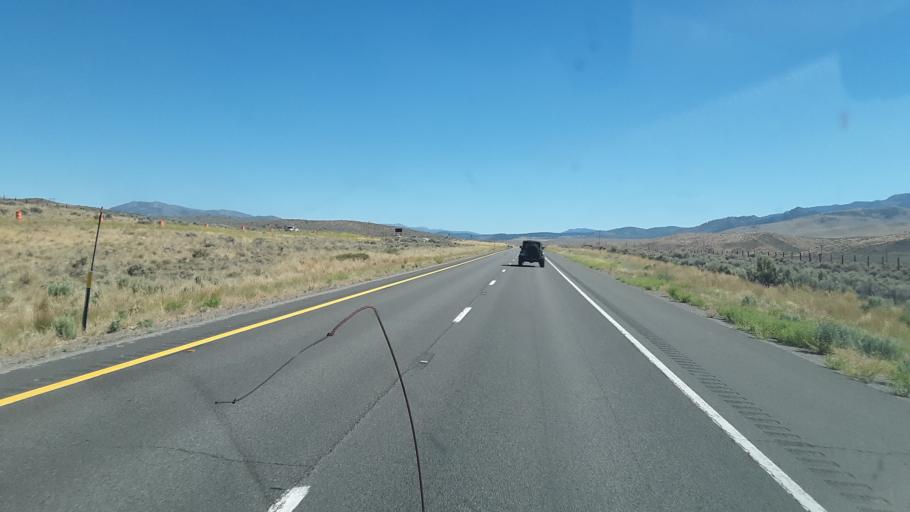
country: US
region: Nevada
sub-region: Washoe County
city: Cold Springs
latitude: 39.7274
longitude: -120.0388
